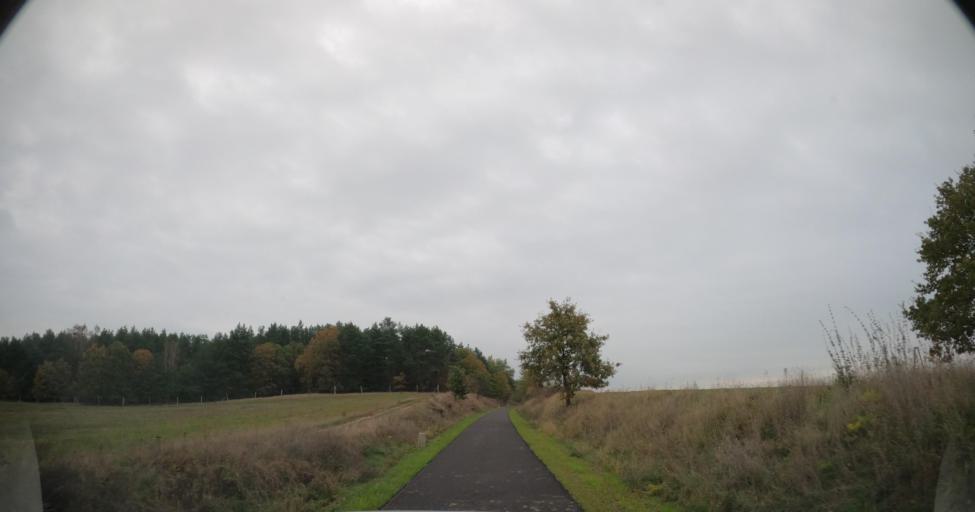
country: PL
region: West Pomeranian Voivodeship
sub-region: Powiat choszczenski
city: Choszczno
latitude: 53.1630
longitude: 15.3793
